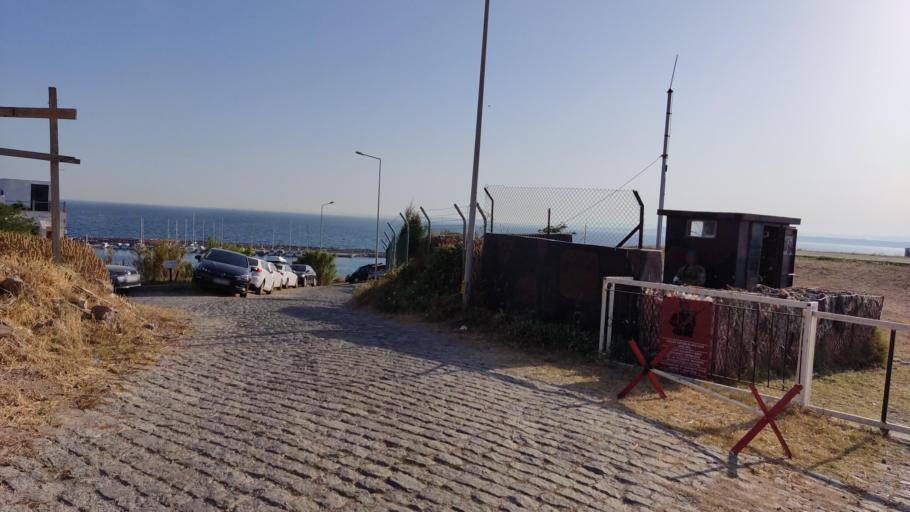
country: TR
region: Canakkale
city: Bozcaada
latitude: 39.8325
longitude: 26.0737
